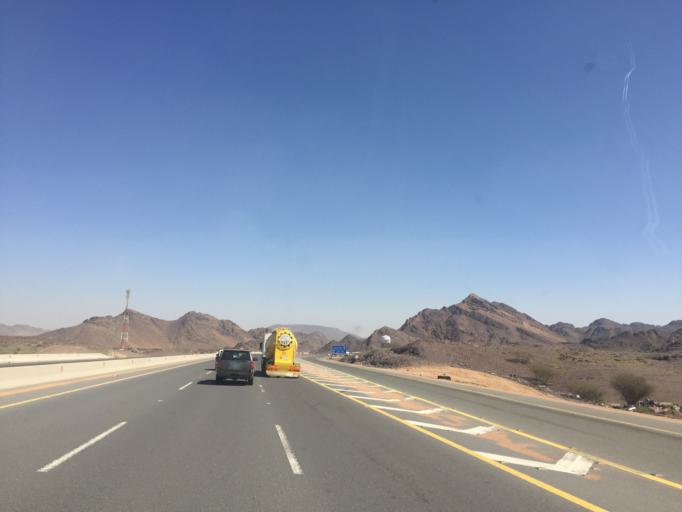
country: SA
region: Al Madinah al Munawwarah
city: Sultanah
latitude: 24.3146
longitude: 39.4230
